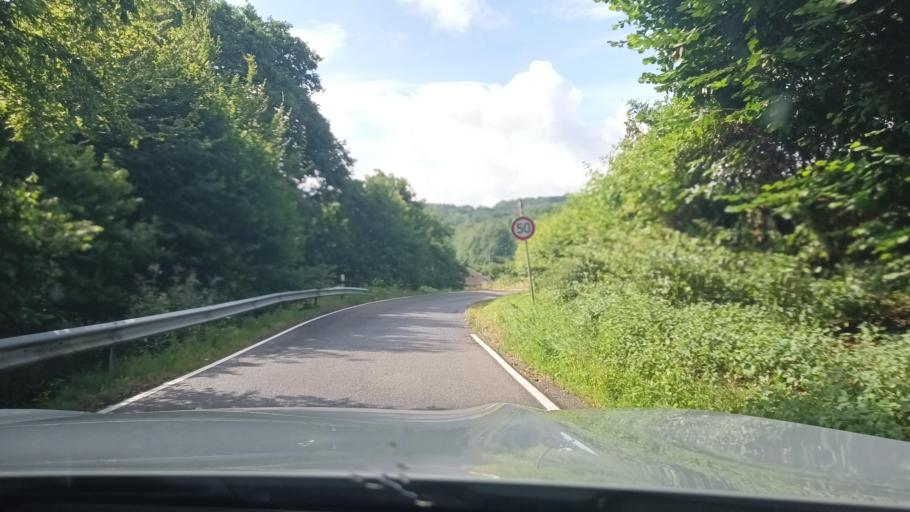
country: DE
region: North Rhine-Westphalia
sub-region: Regierungsbezirk Koln
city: Hennef
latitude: 50.7407
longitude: 7.3138
